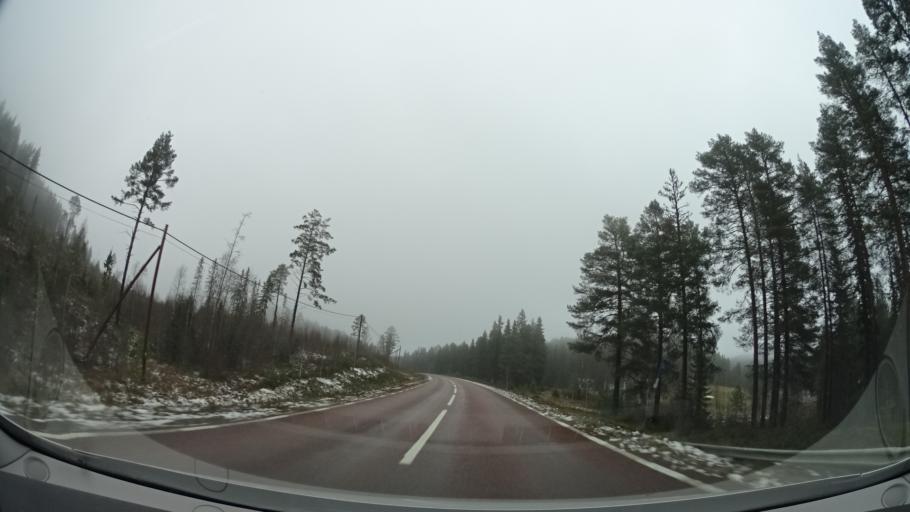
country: SE
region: Vaesterbotten
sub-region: Dorotea Kommun
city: Dorotea
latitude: 64.1509
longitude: 16.2612
